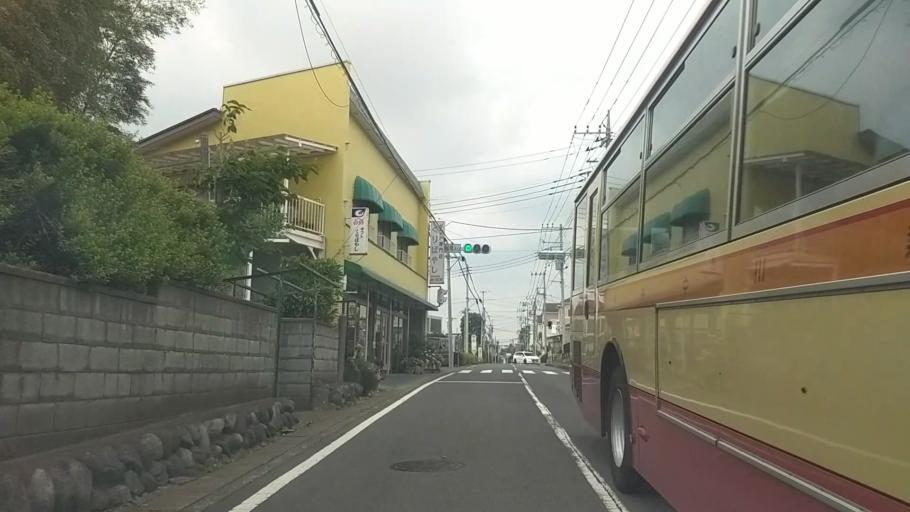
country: JP
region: Kanagawa
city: Atsugi
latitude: 35.3997
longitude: 139.4161
